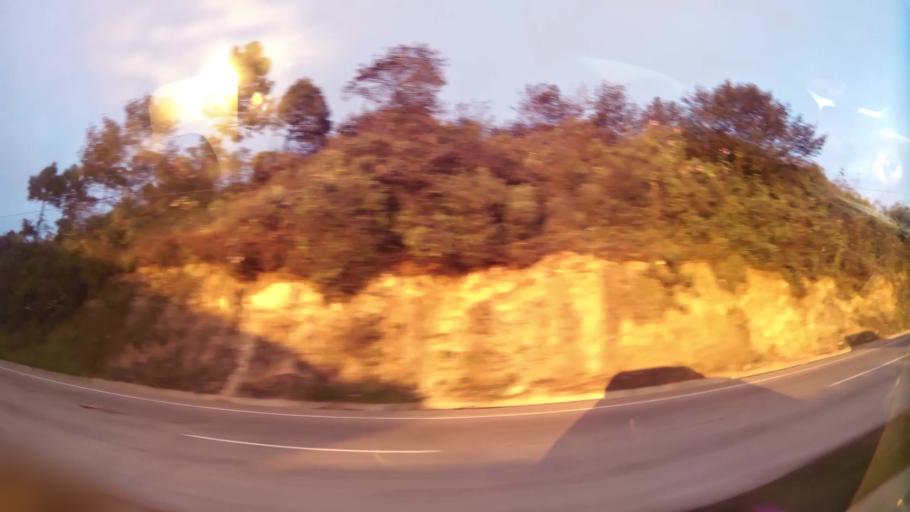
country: GT
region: Solola
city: Concepcion
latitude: 14.8369
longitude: -91.1275
